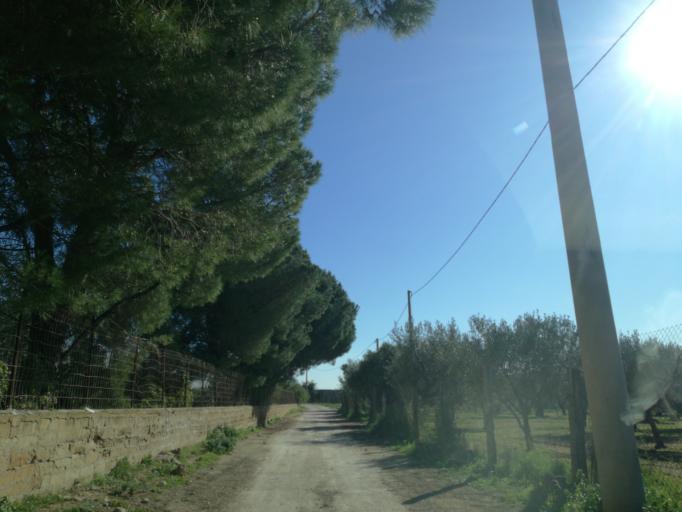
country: IT
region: Sicily
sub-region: Provincia di Caltanissetta
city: Niscemi
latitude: 37.0584
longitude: 14.3584
